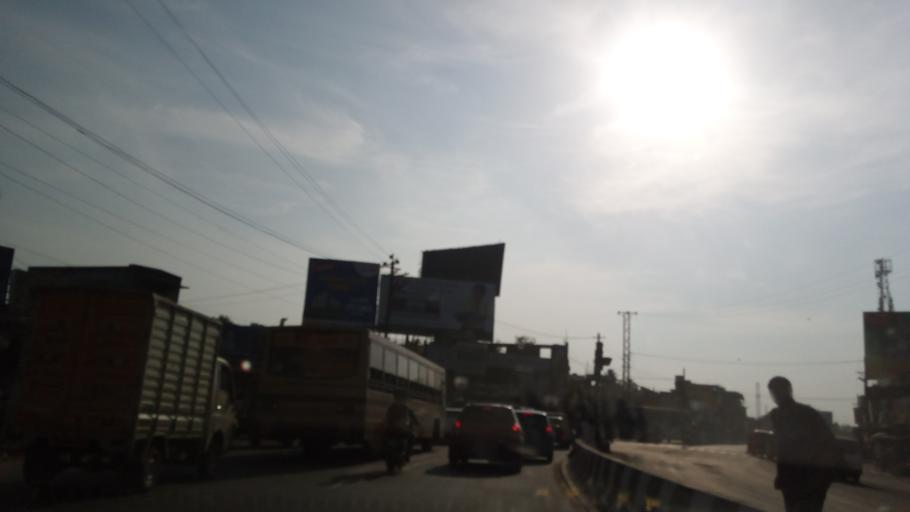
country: IN
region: Tamil Nadu
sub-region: Kancheepuram
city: Poonamalle
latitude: 13.0450
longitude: 80.1162
